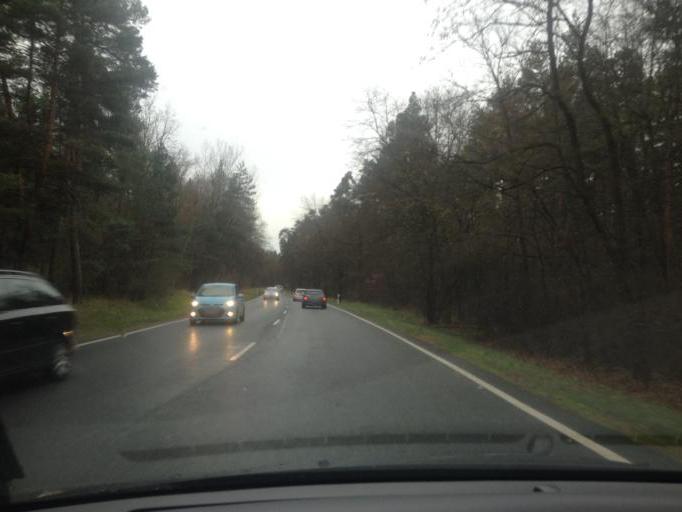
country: DE
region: Bavaria
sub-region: Regierungsbezirk Mittelfranken
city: Wendelstein
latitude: 49.3874
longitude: 11.1102
